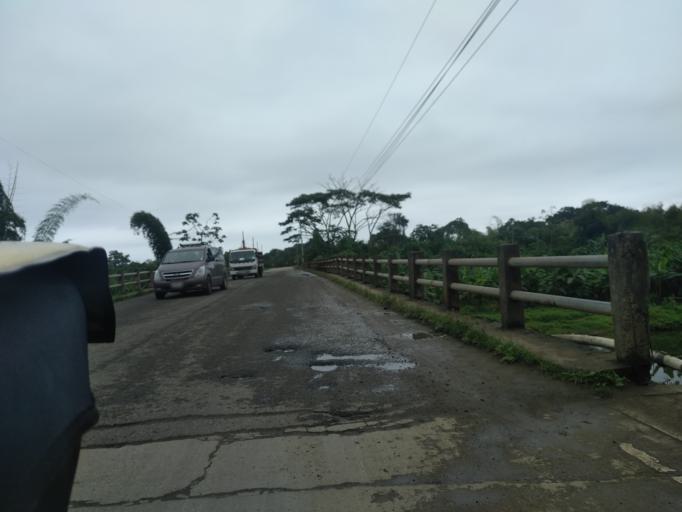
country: EC
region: Manabi
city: Jipijapa
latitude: -1.6726
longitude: -80.8094
